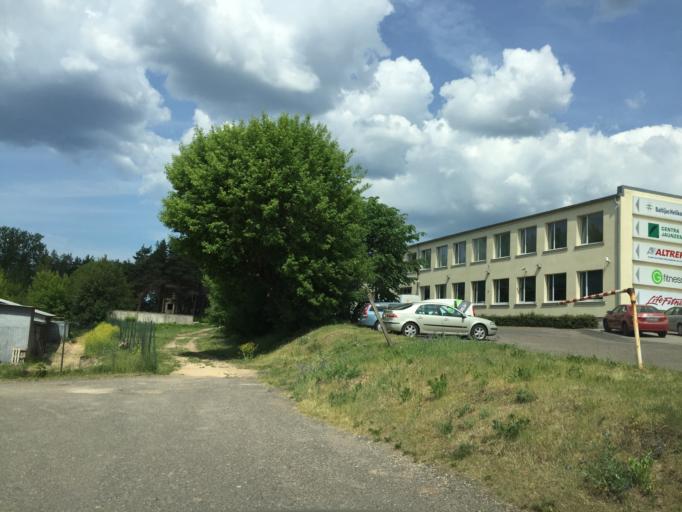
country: LV
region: Riga
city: Bergi
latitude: 56.9970
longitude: 24.2652
